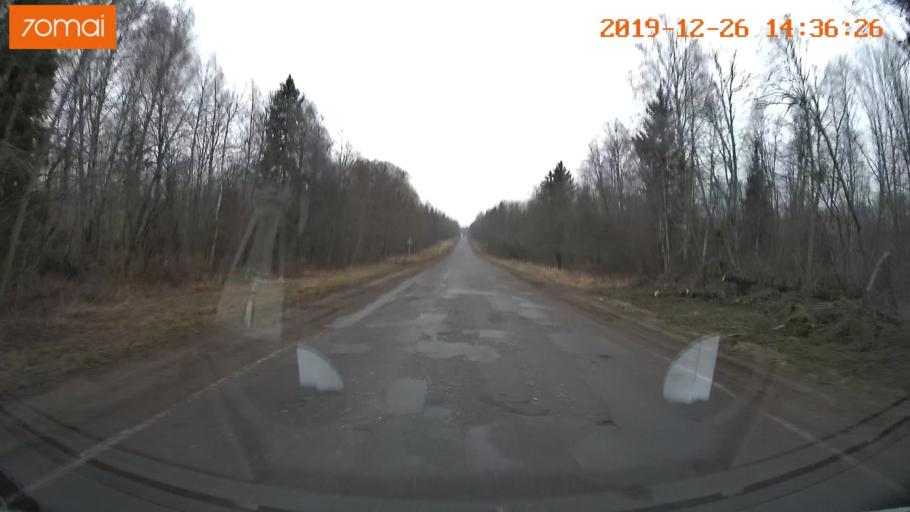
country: RU
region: Jaroslavl
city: Poshekhon'ye
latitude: 58.4114
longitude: 38.9761
